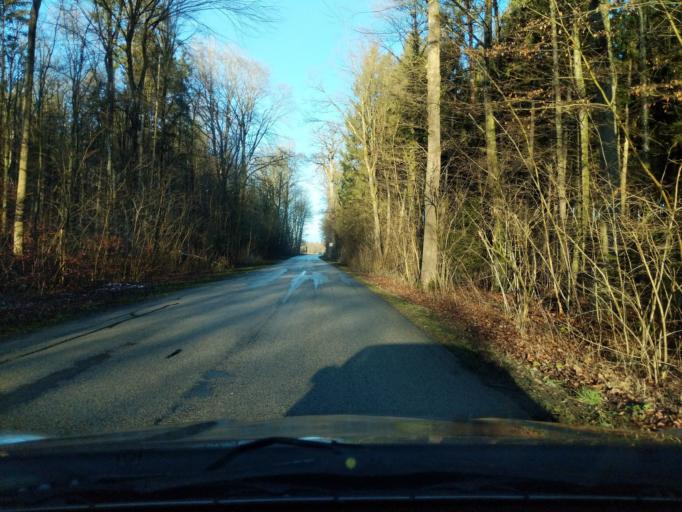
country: DE
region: Bavaria
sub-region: Upper Bavaria
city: Zorneding
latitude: 48.0876
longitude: 11.8498
